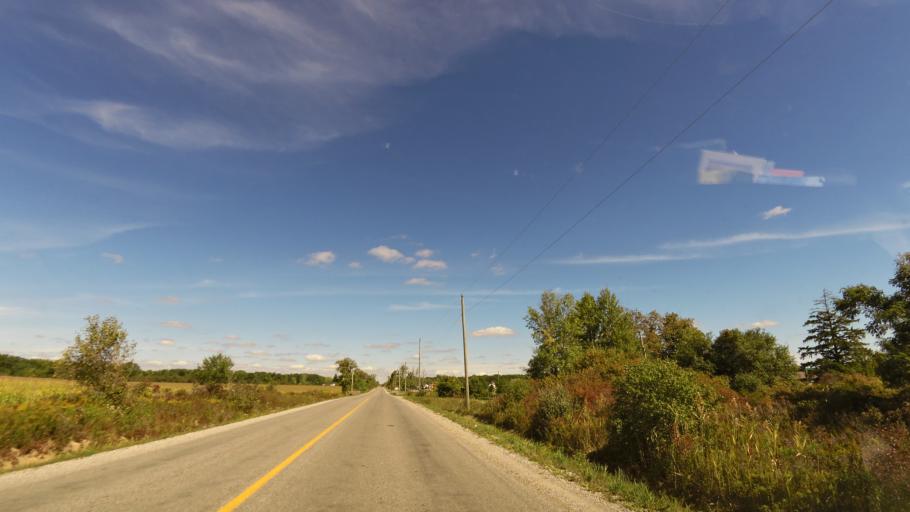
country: CA
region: Ontario
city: Brantford
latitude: 43.0793
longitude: -80.1448
